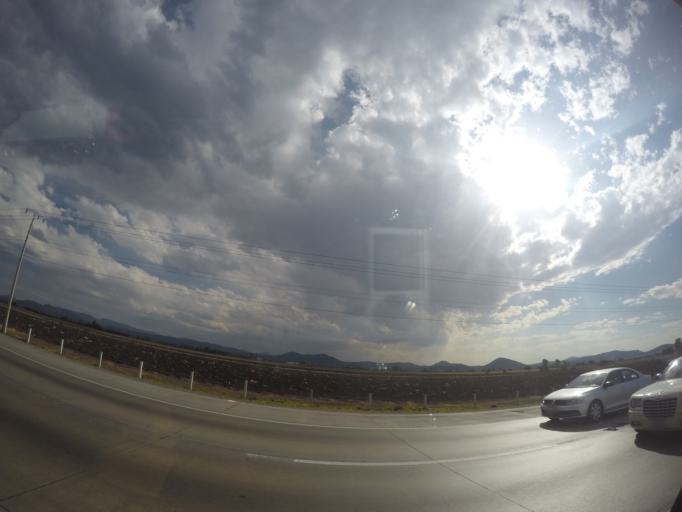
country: MX
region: Queretaro
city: El Sauz
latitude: 20.4626
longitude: -100.0983
